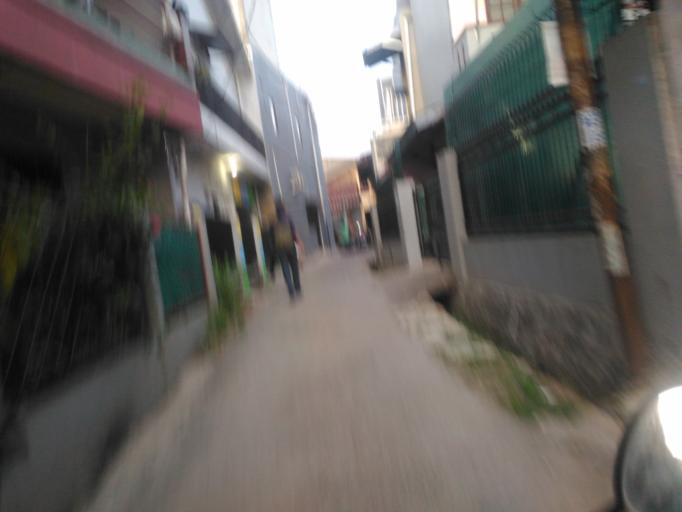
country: ID
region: West Java
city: Depok
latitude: -6.3558
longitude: 106.8407
